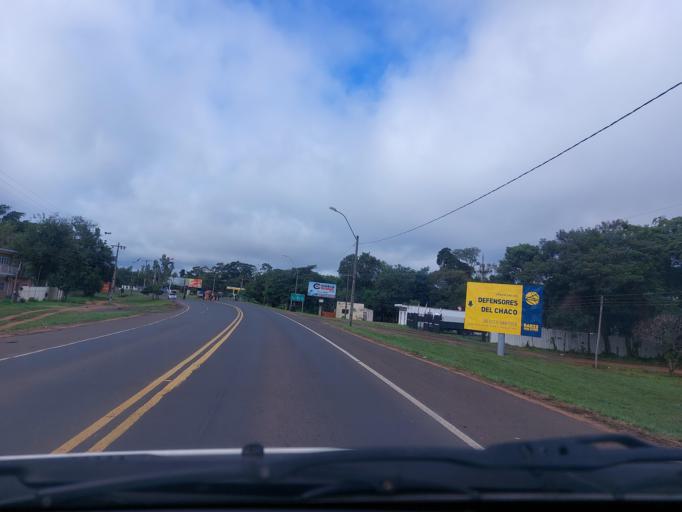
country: PY
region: San Pedro
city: Guayaybi
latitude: -24.5833
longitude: -56.4020
